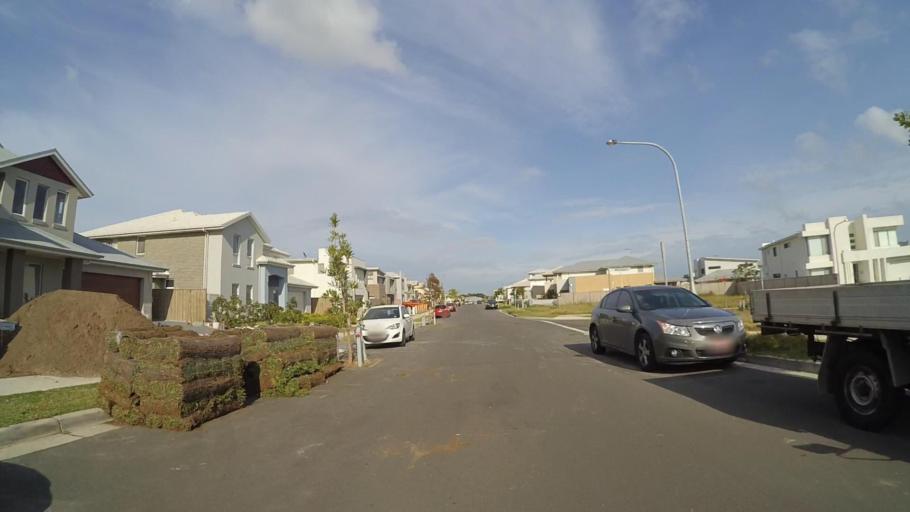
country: AU
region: New South Wales
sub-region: Sutherland Shire
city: Cronulla
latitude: -34.0368
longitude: 151.1646
